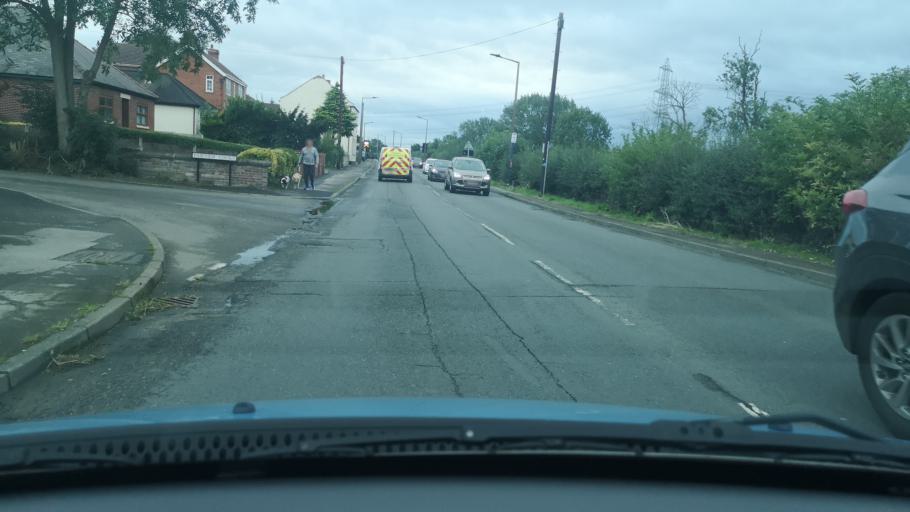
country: GB
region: England
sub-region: Doncaster
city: Kirk Sandall
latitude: 53.5733
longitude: -1.0677
